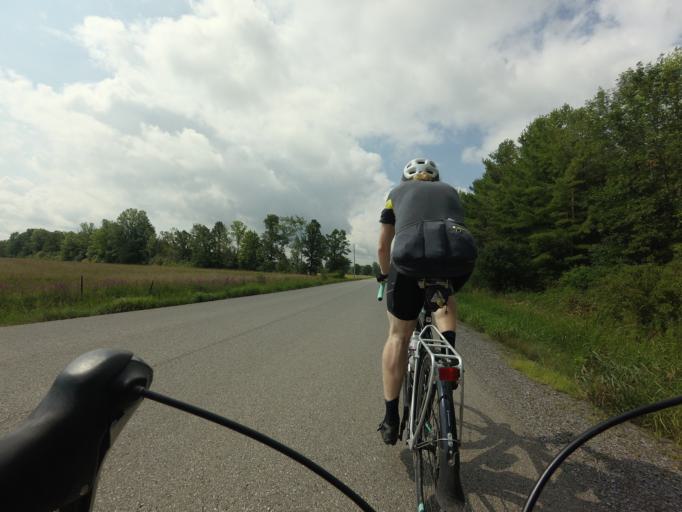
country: CA
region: Ontario
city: Prescott
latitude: 44.8126
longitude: -75.7090
